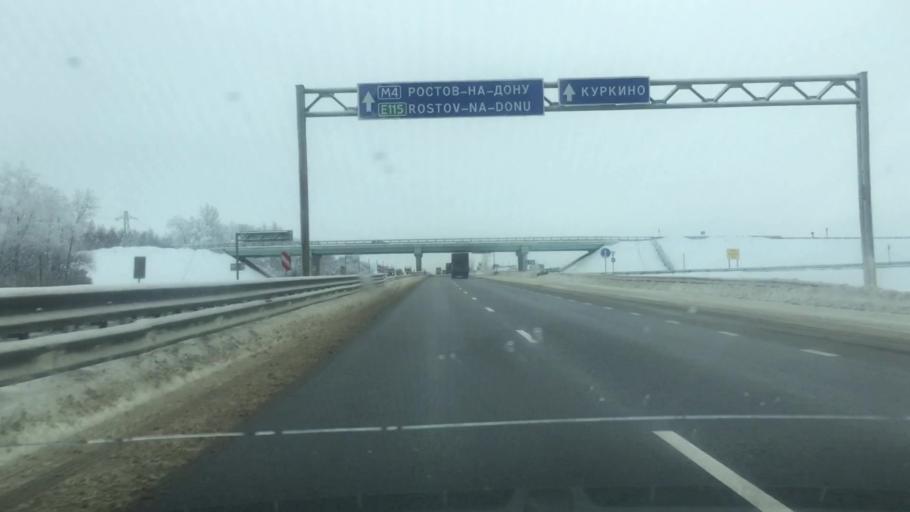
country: RU
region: Tula
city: Kazachka
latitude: 53.3142
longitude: 38.1793
